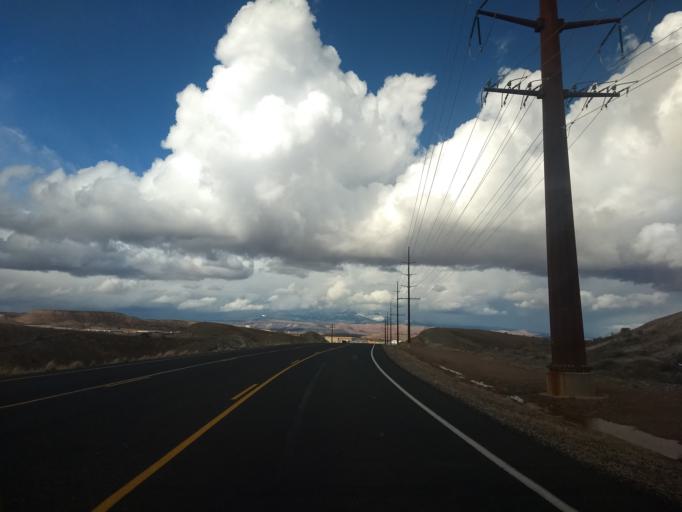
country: US
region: Utah
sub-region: Washington County
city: Saint George
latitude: 37.0176
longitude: -113.5643
